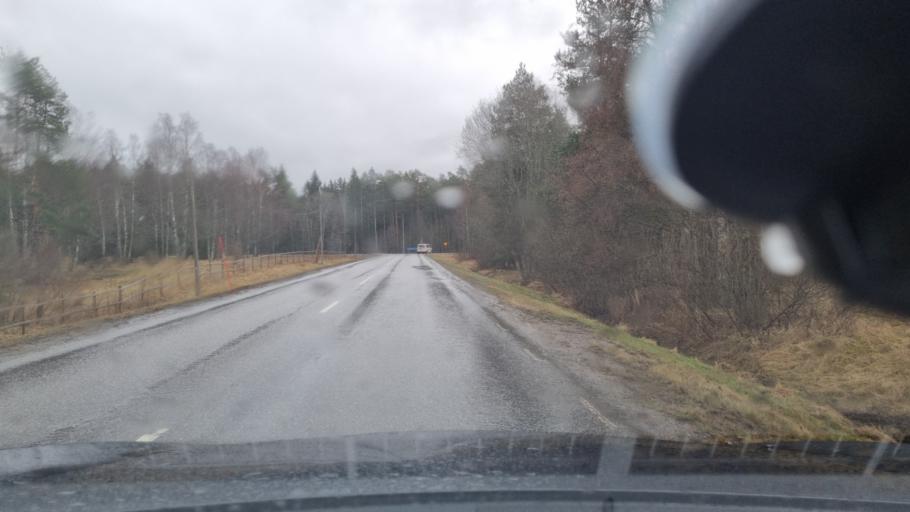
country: SE
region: Stockholm
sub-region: Upplands-Bro Kommun
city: Kungsaengen
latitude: 59.5158
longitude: 17.7594
